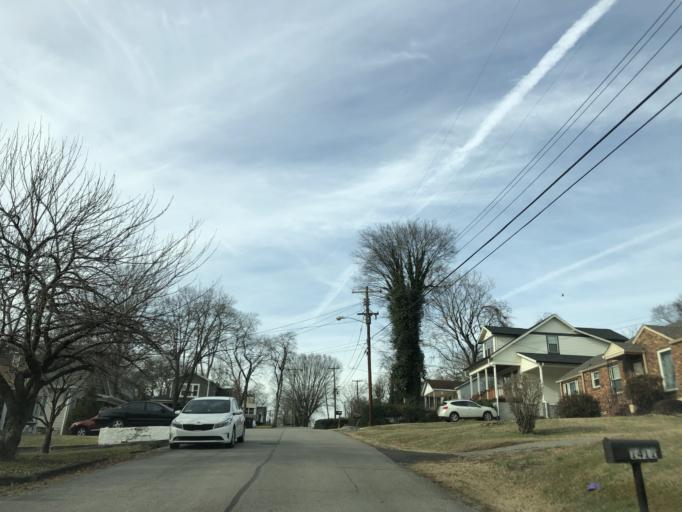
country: US
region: Tennessee
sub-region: Davidson County
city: Nashville
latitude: 36.2153
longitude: -86.7235
